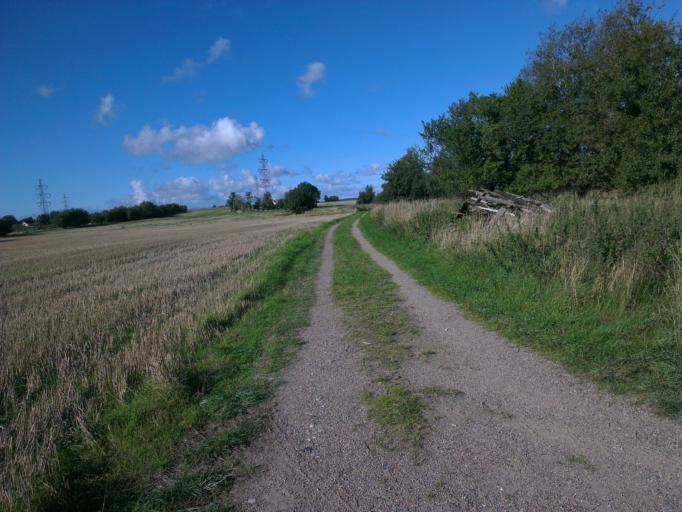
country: DK
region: Capital Region
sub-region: Frederikssund Kommune
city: Frederikssund
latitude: 55.7922
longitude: 12.0425
